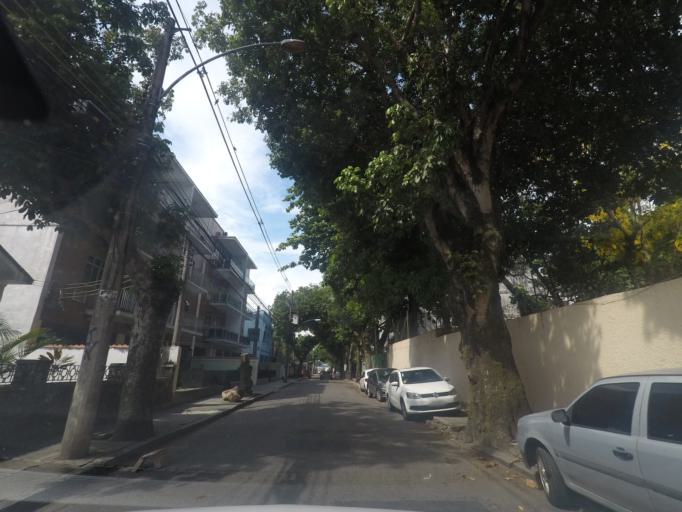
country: BR
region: Rio de Janeiro
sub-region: Rio De Janeiro
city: Rio de Janeiro
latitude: -22.8223
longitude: -43.1747
